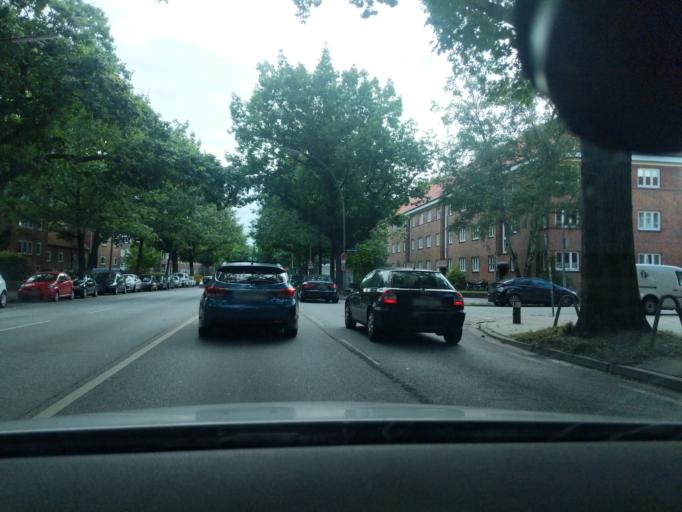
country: DE
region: Hamburg
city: Altona
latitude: 53.5540
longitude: 9.9143
